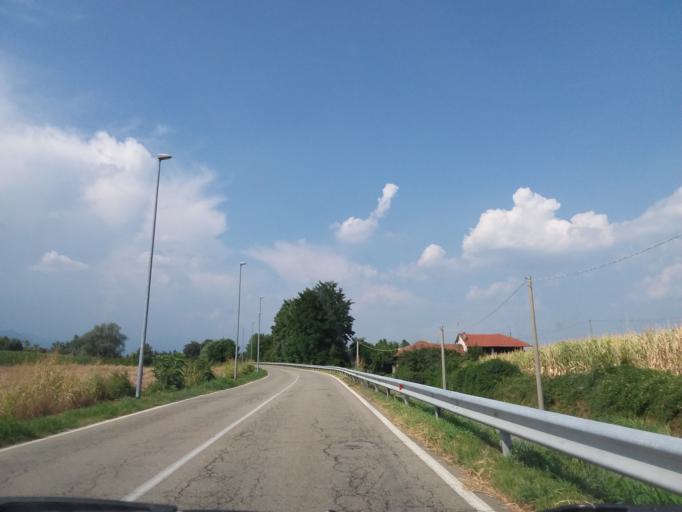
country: IT
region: Piedmont
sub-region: Provincia di Torino
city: Rivoli
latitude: 45.0788
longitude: 7.5424
